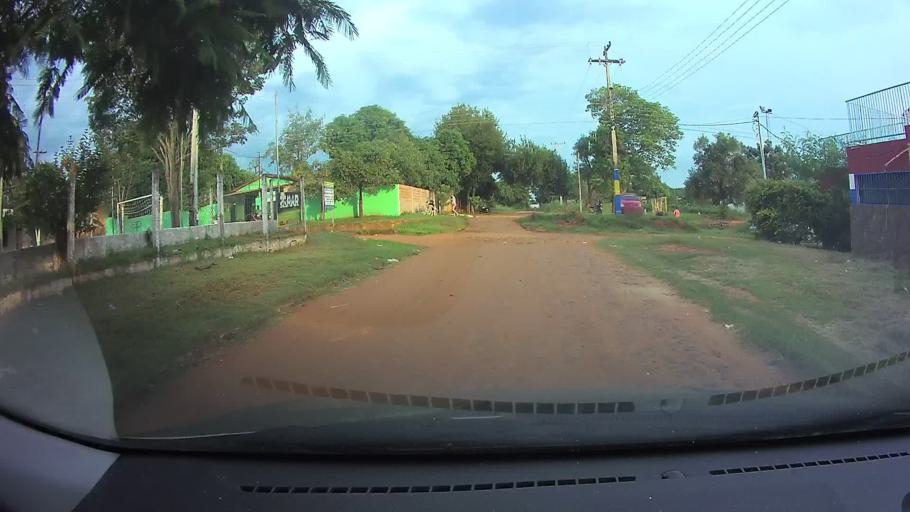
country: PY
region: Central
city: Limpio
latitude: -25.2453
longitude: -57.4556
